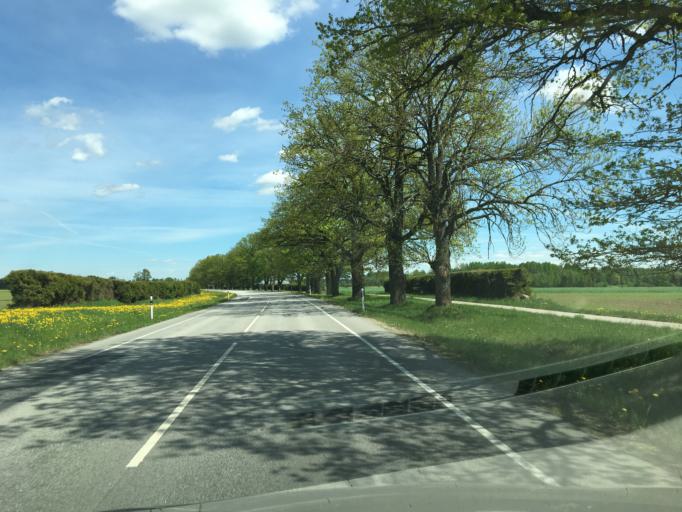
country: EE
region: Vorumaa
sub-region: Antsla vald
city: Vana-Antsla
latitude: 57.9053
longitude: 26.2886
